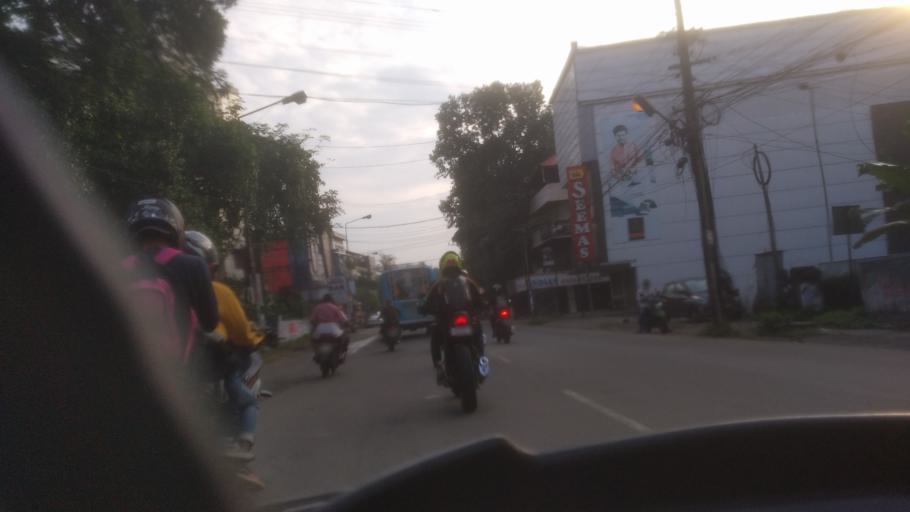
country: IN
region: Kerala
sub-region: Ernakulam
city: Perumpavur
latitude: 10.1148
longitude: 76.4708
